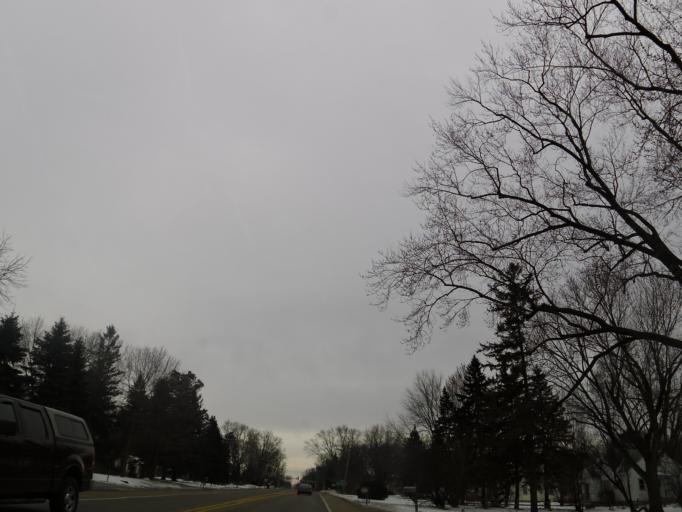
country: US
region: Minnesota
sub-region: Washington County
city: Oakdale
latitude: 44.9732
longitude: -92.9849
